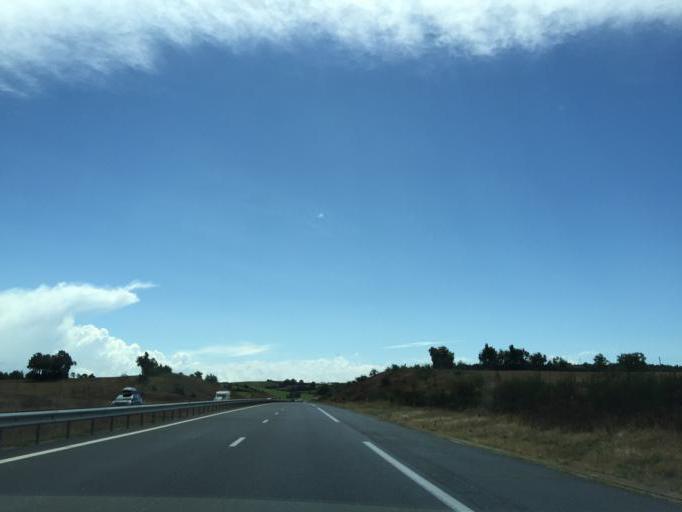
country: FR
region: Midi-Pyrenees
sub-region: Departement de l'Aveyron
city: Severac-le-Chateau
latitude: 44.2860
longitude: 3.0934
